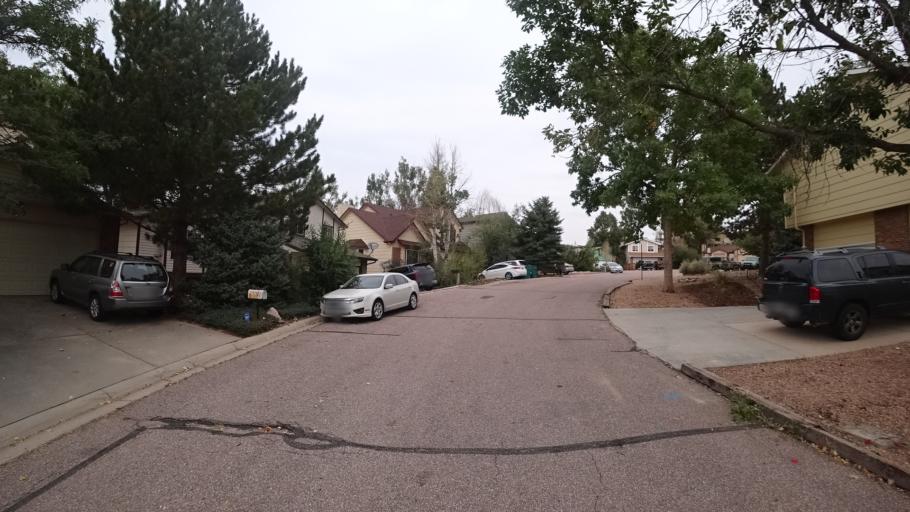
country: US
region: Colorado
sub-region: El Paso County
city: Cimarron Hills
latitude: 38.9089
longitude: -104.7351
